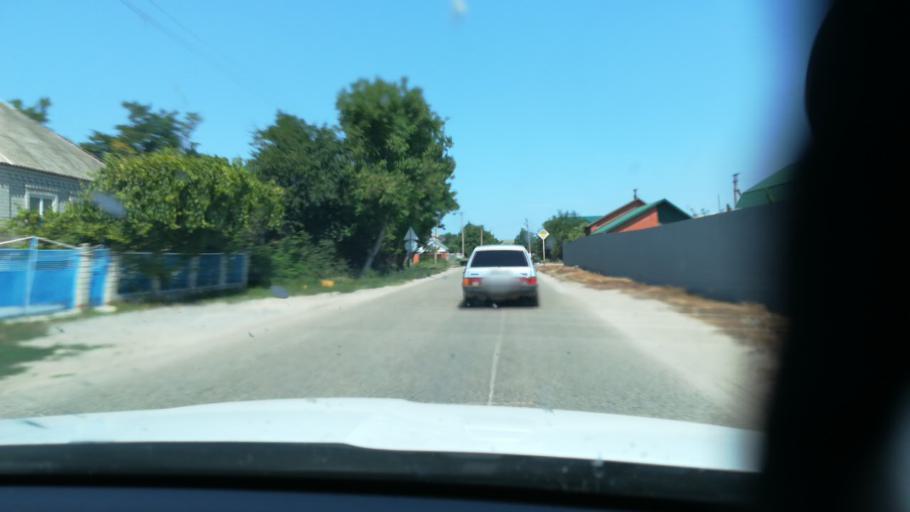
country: RU
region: Krasnodarskiy
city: Starotitarovskaya
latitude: 45.2067
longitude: 37.1465
